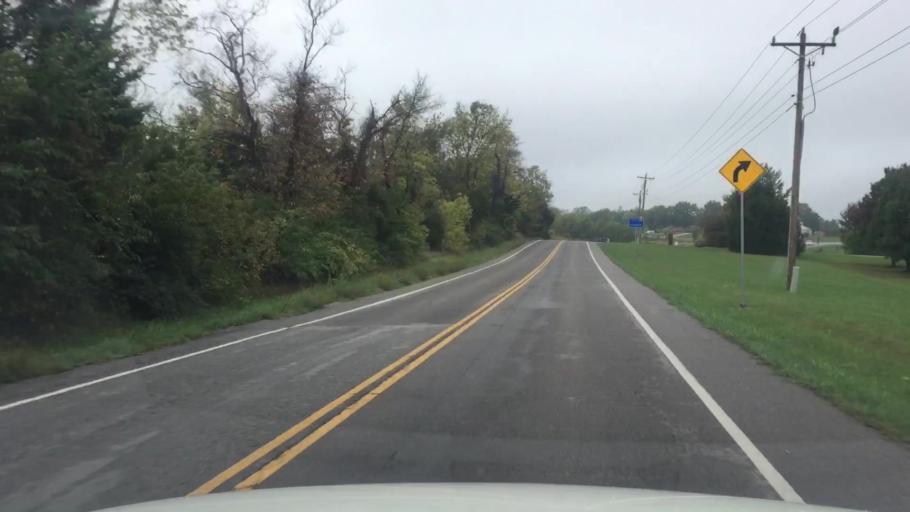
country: US
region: Missouri
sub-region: Boone County
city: Columbia
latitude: 38.8698
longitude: -92.3951
